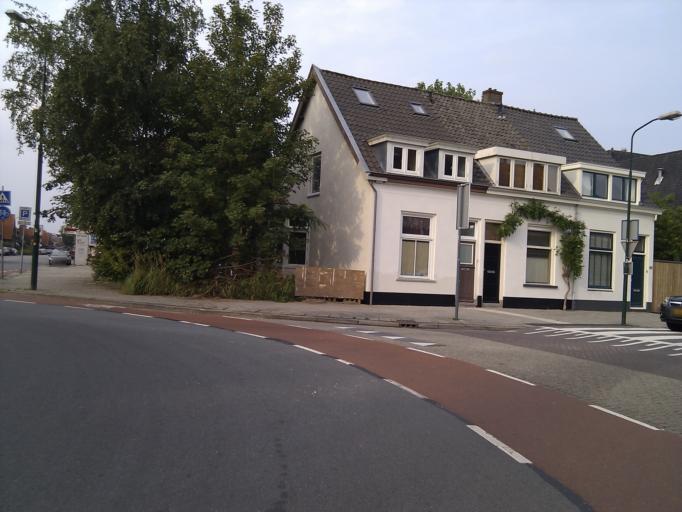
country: NL
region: Utrecht
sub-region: Gemeente De Bilt
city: De Bilt
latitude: 52.1054
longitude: 5.1783
